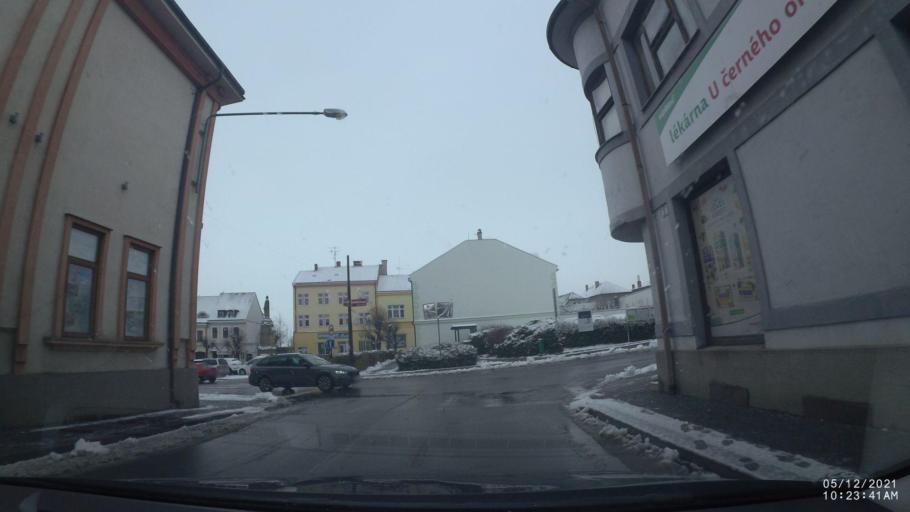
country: CZ
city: Vamberk
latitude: 50.1175
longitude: 16.2909
